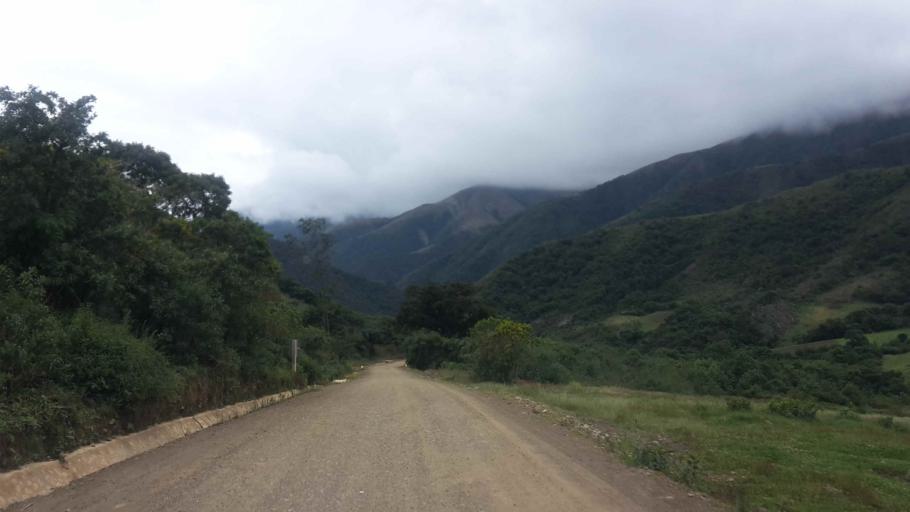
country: BO
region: Cochabamba
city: Totora
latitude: -17.5706
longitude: -65.2814
